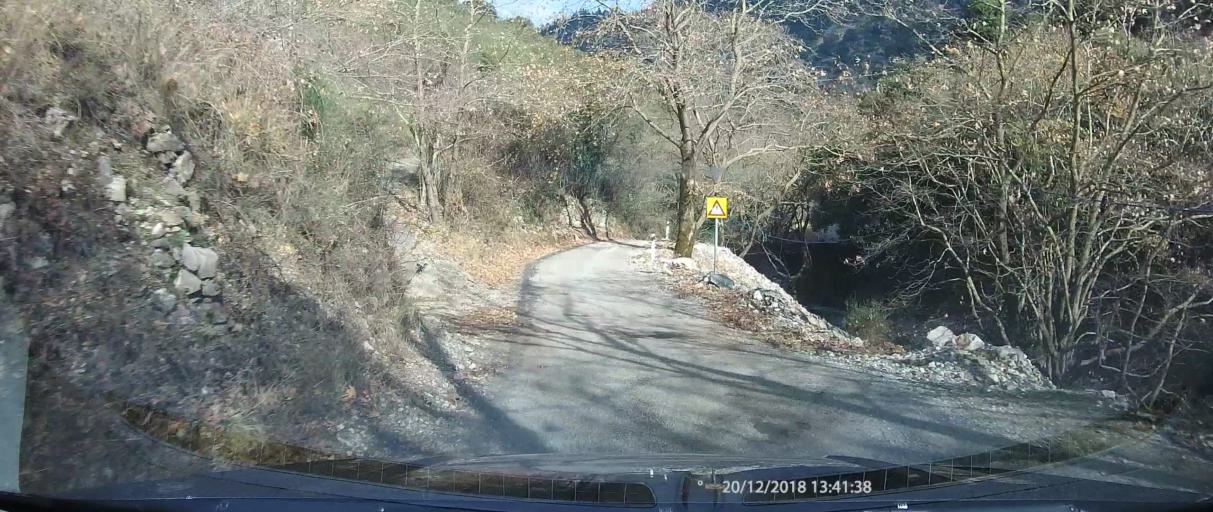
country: GR
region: West Greece
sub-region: Nomos Aitolias kai Akarnanias
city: Thermo
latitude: 38.6500
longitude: 21.6153
